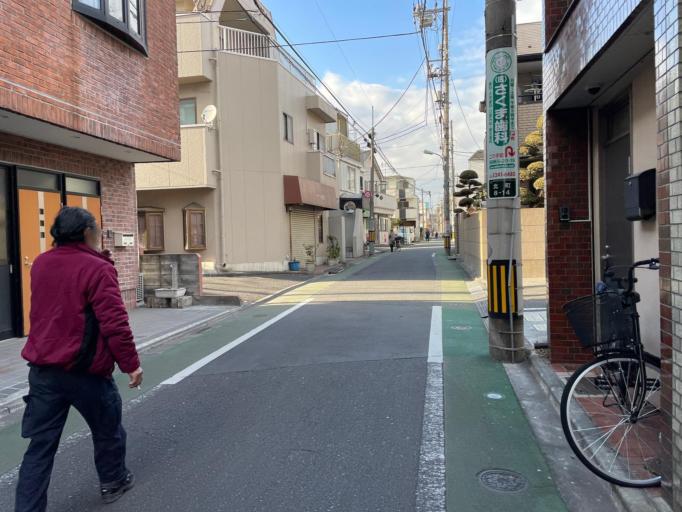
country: JP
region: Saitama
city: Wako
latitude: 35.7659
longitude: 139.6479
